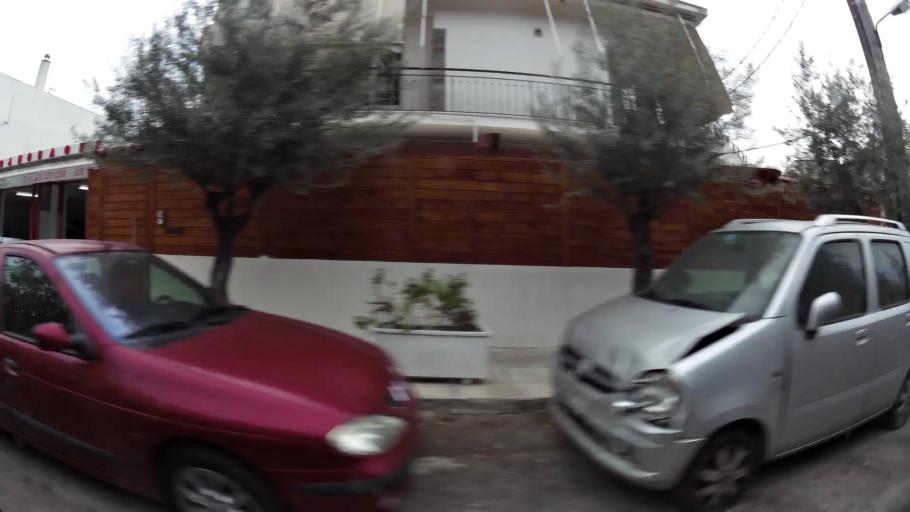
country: GR
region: Attica
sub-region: Nomarchia Athinas
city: Chaidari
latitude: 38.0079
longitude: 23.6516
